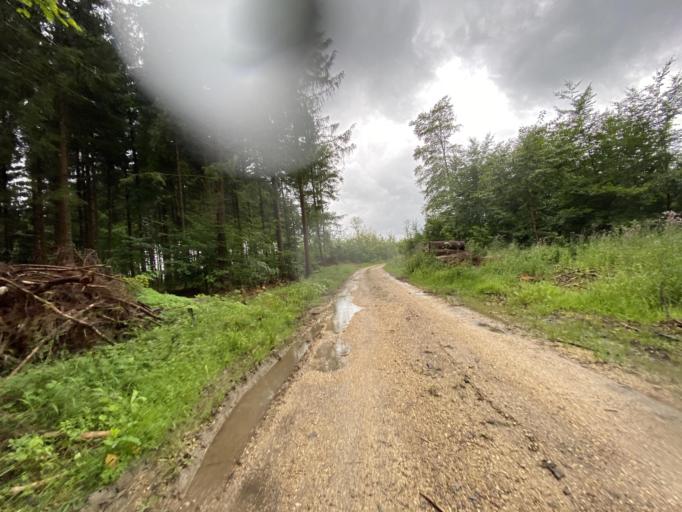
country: DE
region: Baden-Wuerttemberg
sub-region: Tuebingen Region
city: Sigmaringen
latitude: 48.1174
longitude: 9.2301
